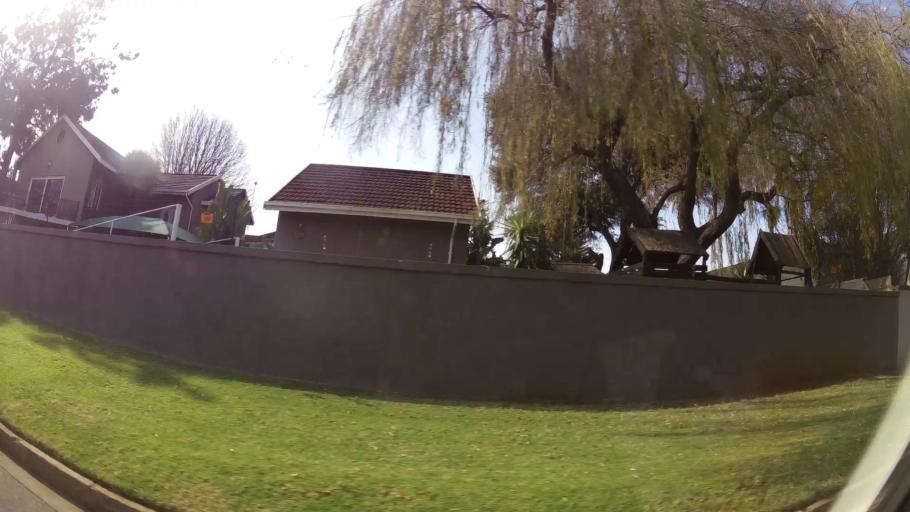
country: ZA
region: Gauteng
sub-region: Ekurhuleni Metropolitan Municipality
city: Boksburg
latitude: -26.1977
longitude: 28.2383
